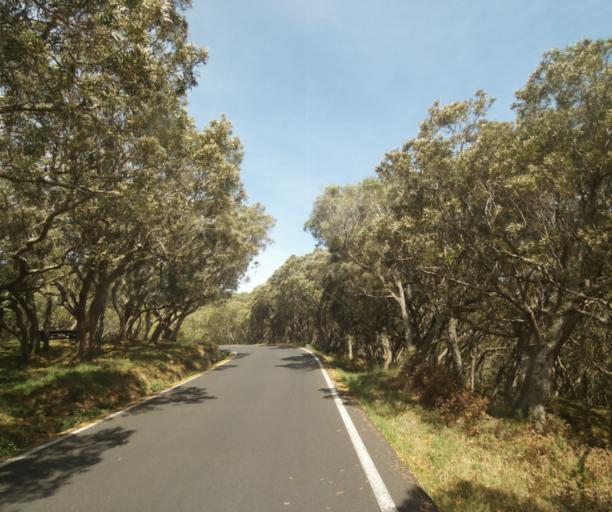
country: RE
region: Reunion
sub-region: Reunion
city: Trois-Bassins
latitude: -21.0612
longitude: 55.3762
